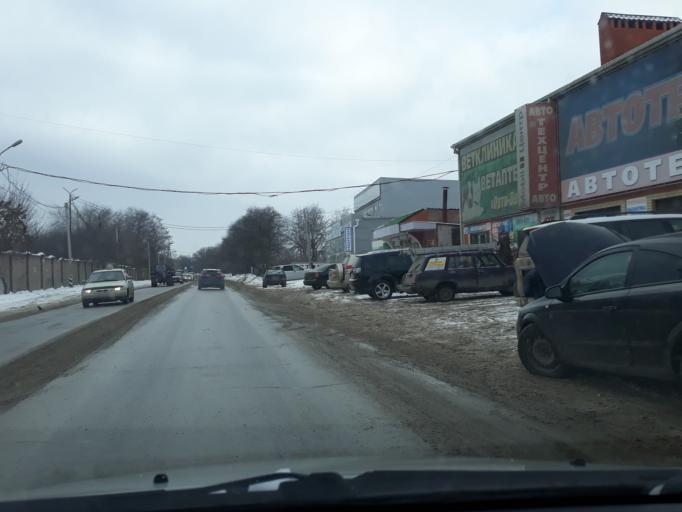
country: RU
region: Rostov
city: Taganrog
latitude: 47.2593
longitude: 38.9099
